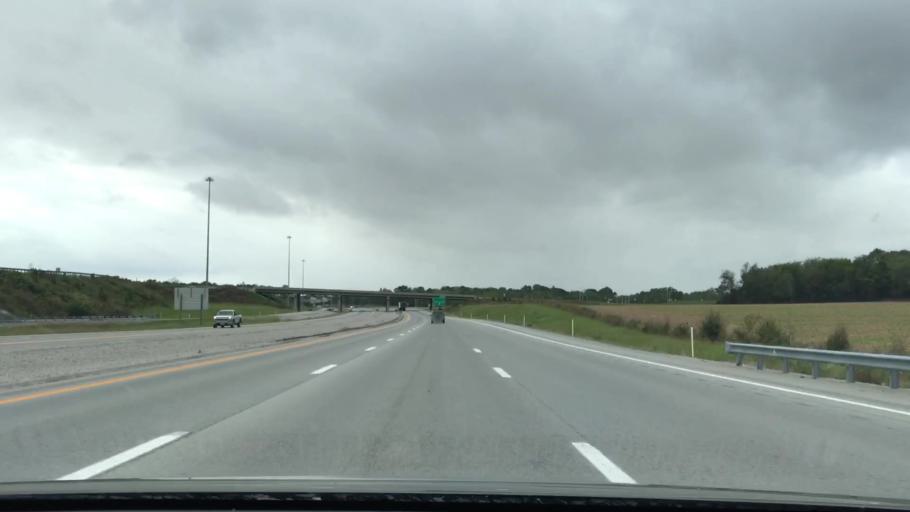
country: US
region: Kentucky
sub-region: Christian County
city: Hopkinsville
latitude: 36.8137
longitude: -87.4863
